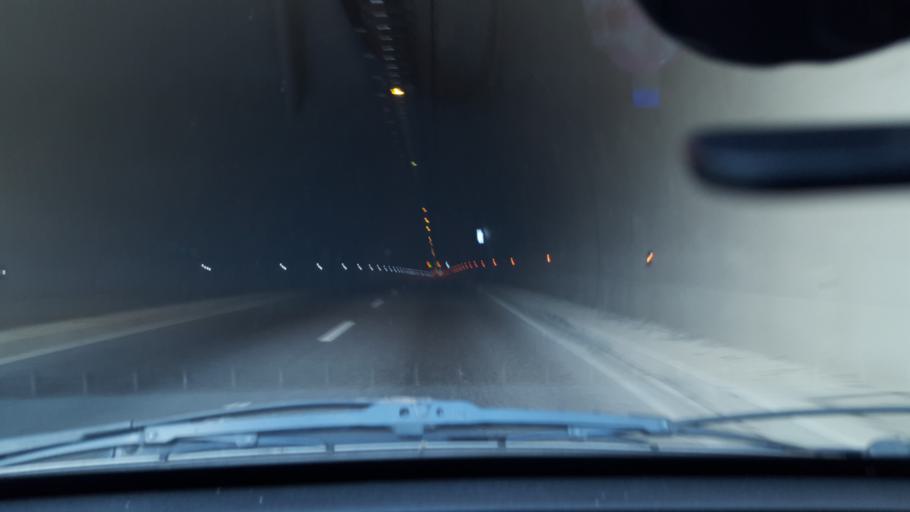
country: AL
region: Tirane
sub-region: Rrethi i Tiranes
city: Krrabe
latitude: 41.1959
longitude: 19.9862
